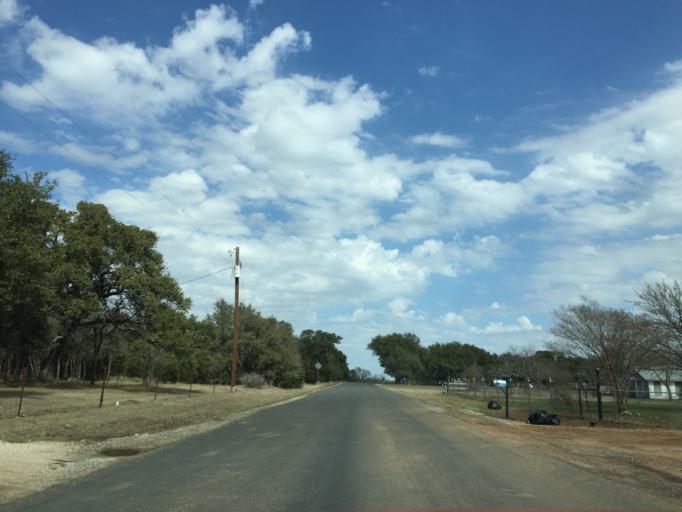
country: US
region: Texas
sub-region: Burnet County
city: Bertram
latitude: 30.7494
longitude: -97.9403
